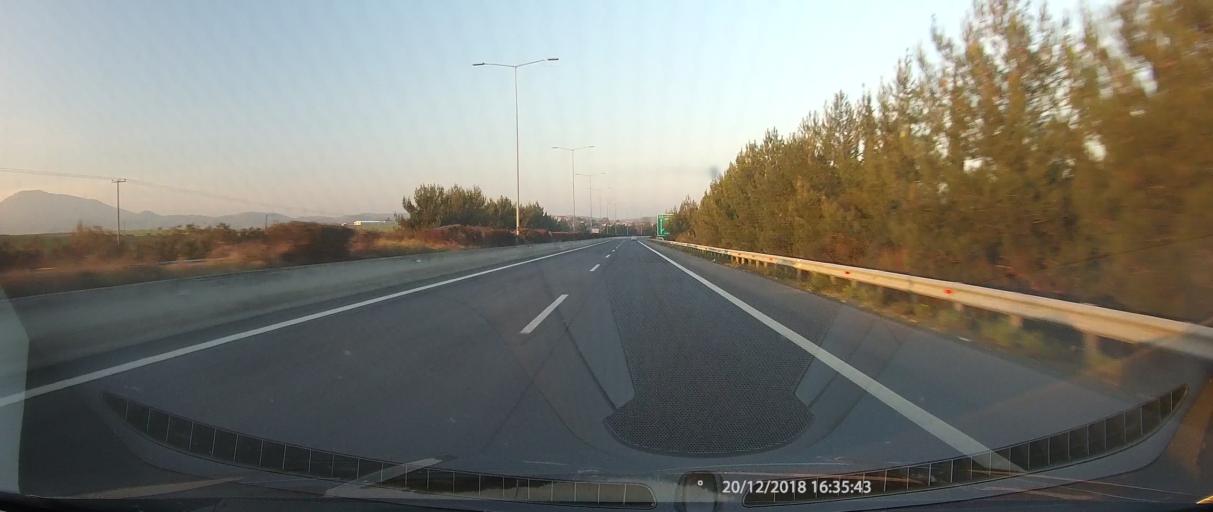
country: GR
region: Thessaly
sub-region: Nomos Magnisias
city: Nea Anchialos
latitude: 39.3082
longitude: 22.7495
